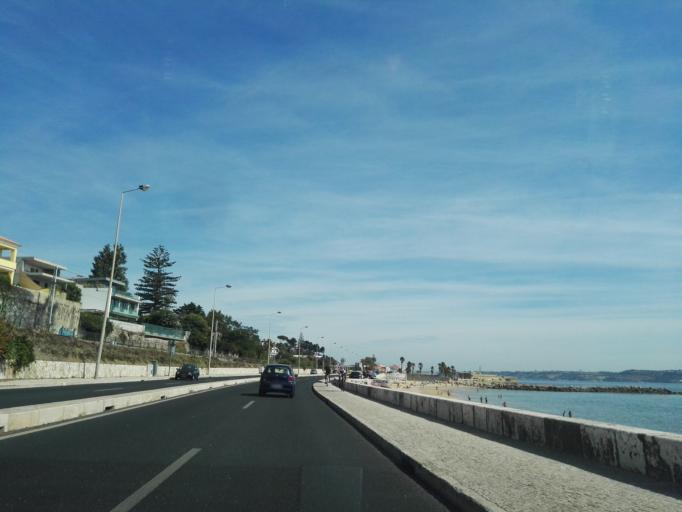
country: PT
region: Lisbon
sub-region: Oeiras
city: Terrugem
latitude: 38.6988
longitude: -9.2801
